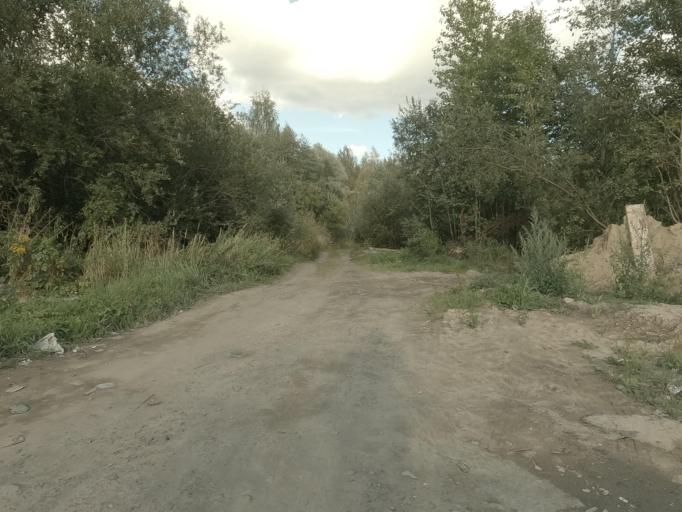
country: RU
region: Leningrad
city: Mga
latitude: 59.7483
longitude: 31.0980
